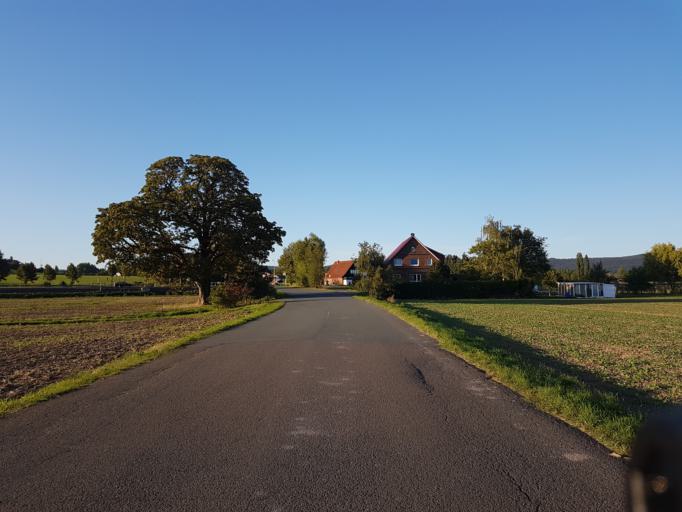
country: DE
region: North Rhine-Westphalia
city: Porta Westfalica
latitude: 52.1944
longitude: 8.9799
